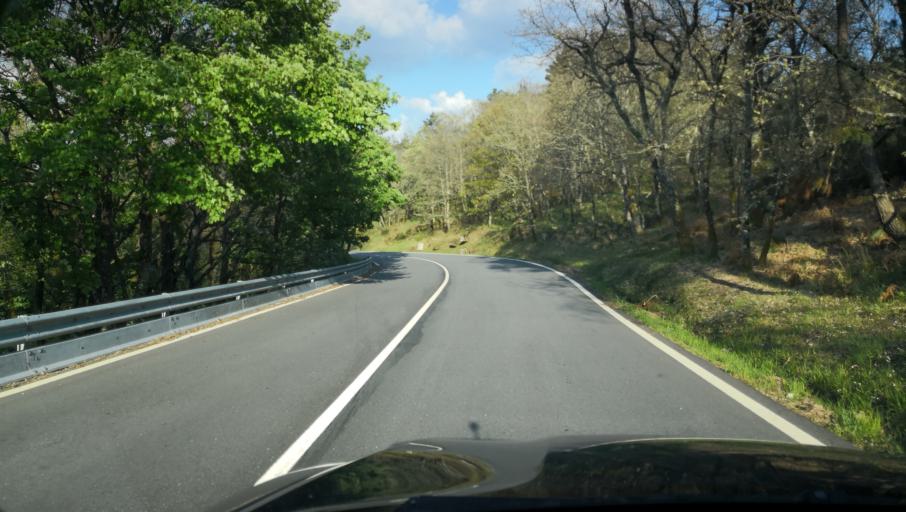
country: PT
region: Vila Real
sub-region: Santa Marta de Penaguiao
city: Santa Marta de Penaguiao
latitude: 41.2824
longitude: -7.8232
